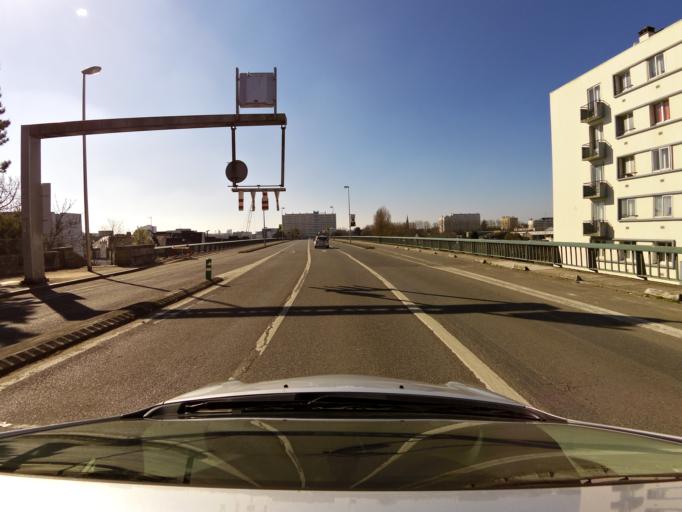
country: FR
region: Brittany
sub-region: Departement du Morbihan
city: Lorient
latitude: 47.7566
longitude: -3.3717
